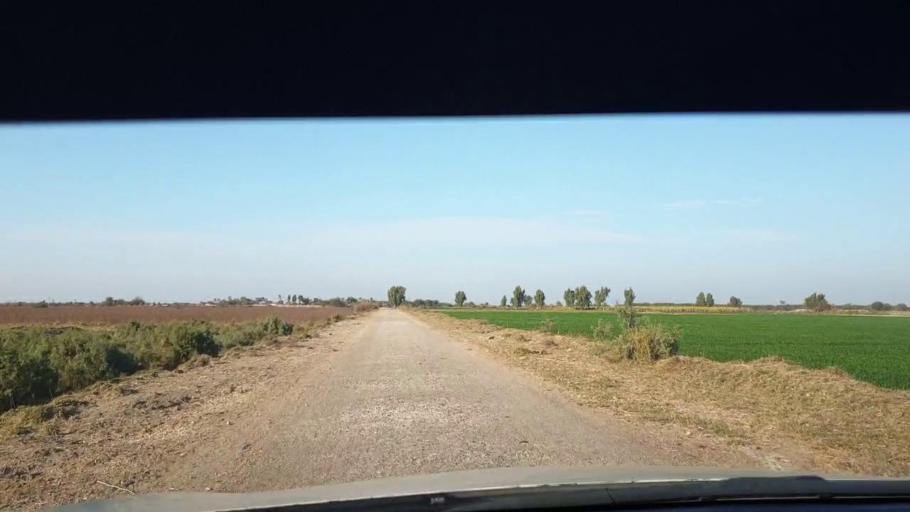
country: PK
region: Sindh
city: Berani
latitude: 25.8168
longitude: 68.9099
